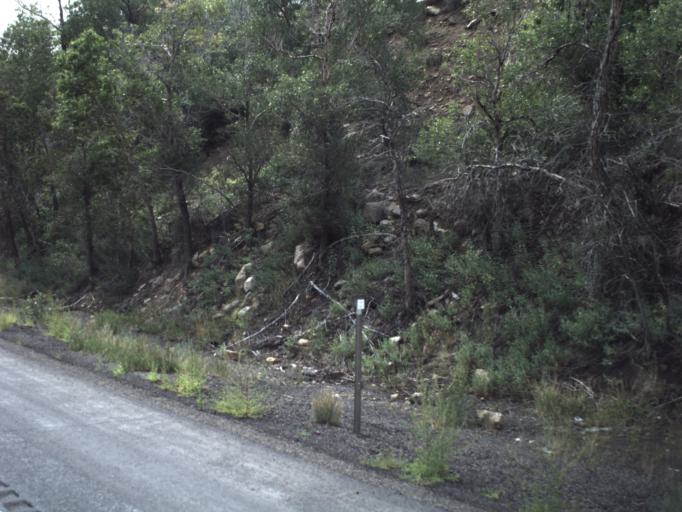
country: US
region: Utah
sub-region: Carbon County
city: Helper
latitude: 39.7632
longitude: -110.8968
